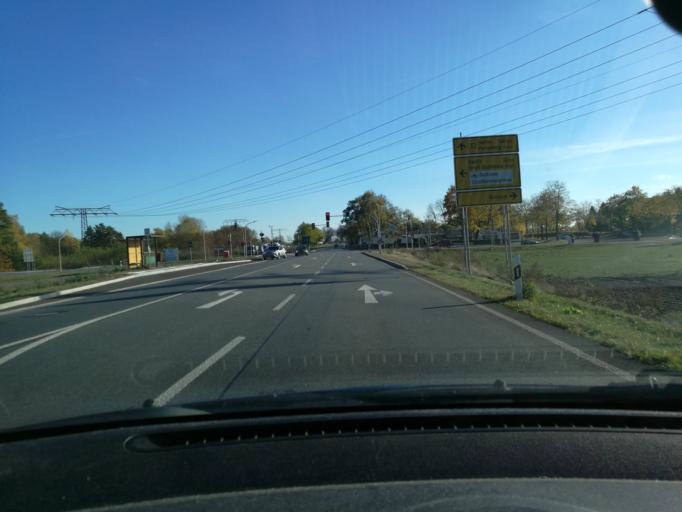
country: DE
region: Brandenburg
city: Perleberg
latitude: 53.1026
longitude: 11.8301
